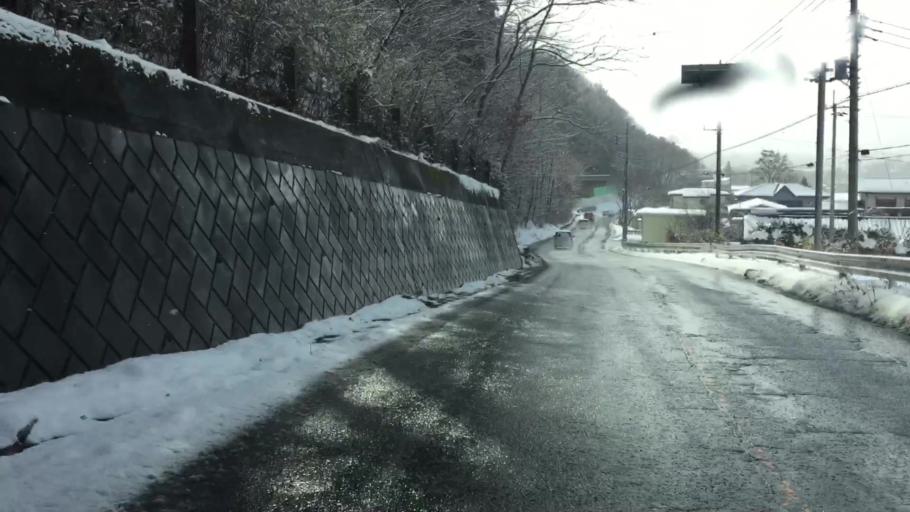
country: JP
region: Gunma
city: Numata
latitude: 36.6790
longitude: 139.0636
